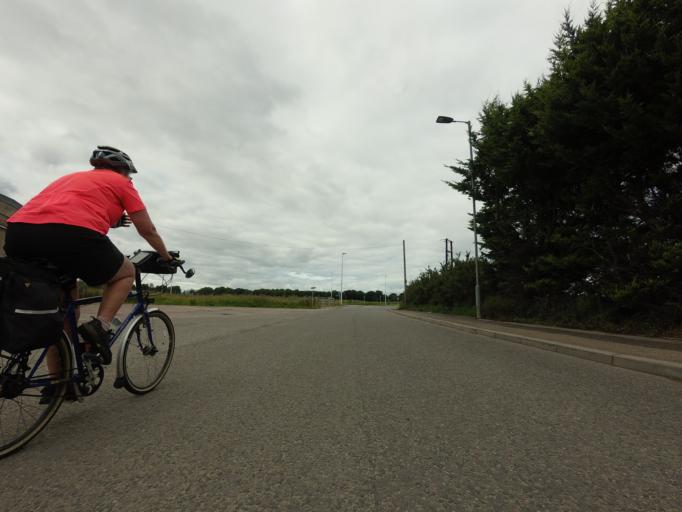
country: GB
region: Scotland
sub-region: Moray
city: Forres
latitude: 57.6134
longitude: -3.6241
